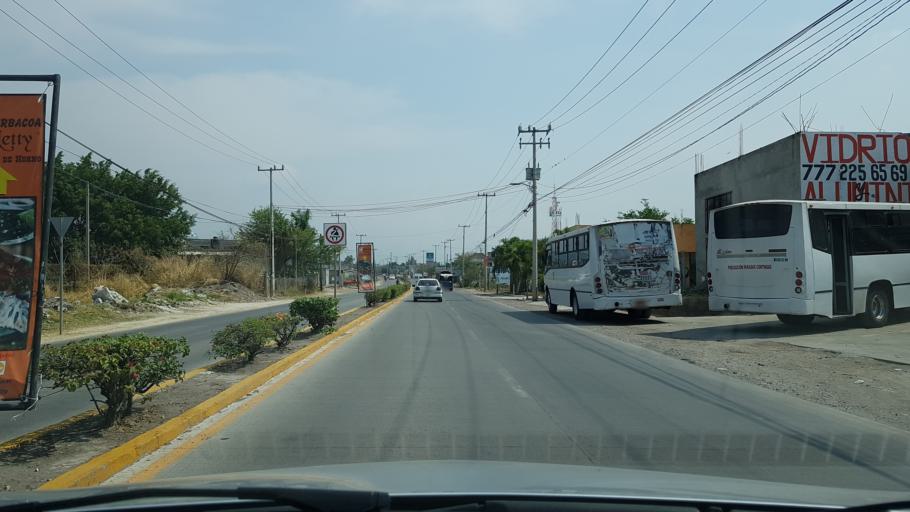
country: MX
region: Morelos
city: Emiliano Zapata
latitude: 18.8101
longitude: -99.1939
